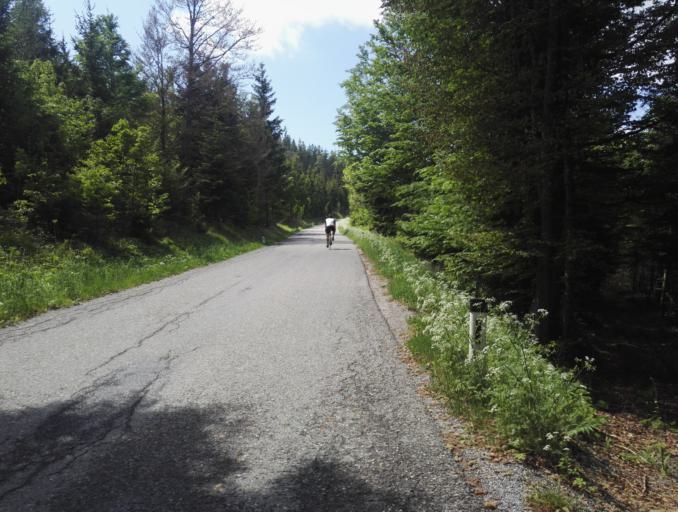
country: AT
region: Styria
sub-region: Politischer Bezirk Weiz
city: Stenzengreith
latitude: 47.2136
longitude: 15.4927
